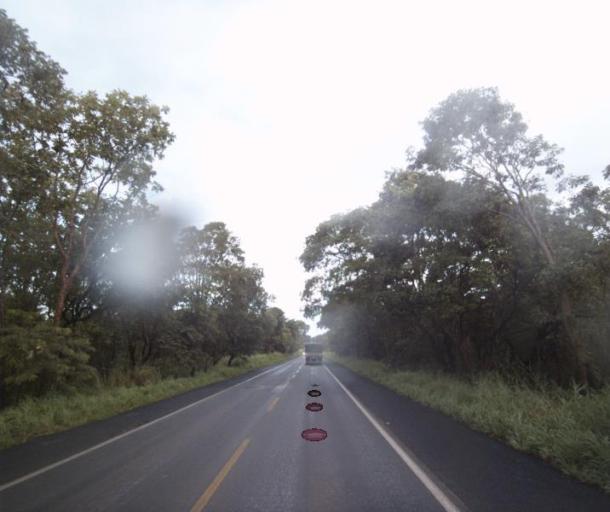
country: BR
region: Goias
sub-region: Porangatu
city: Porangatu
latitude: -13.9058
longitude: -49.0628
